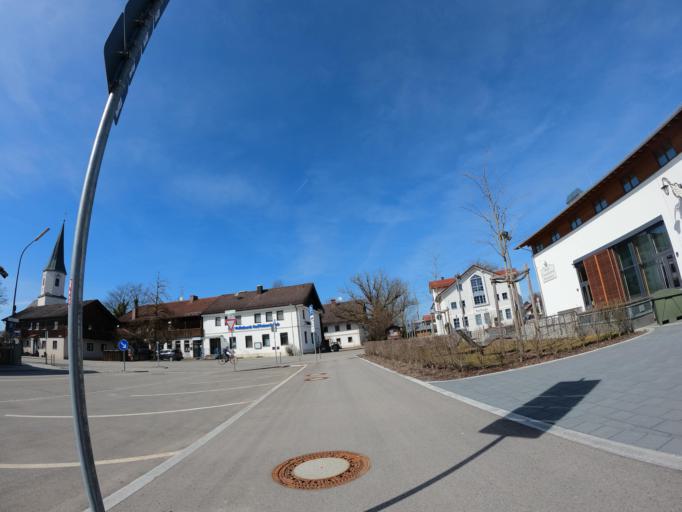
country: DE
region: Bavaria
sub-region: Upper Bavaria
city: Brunnthal
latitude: 48.0064
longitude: 11.6846
